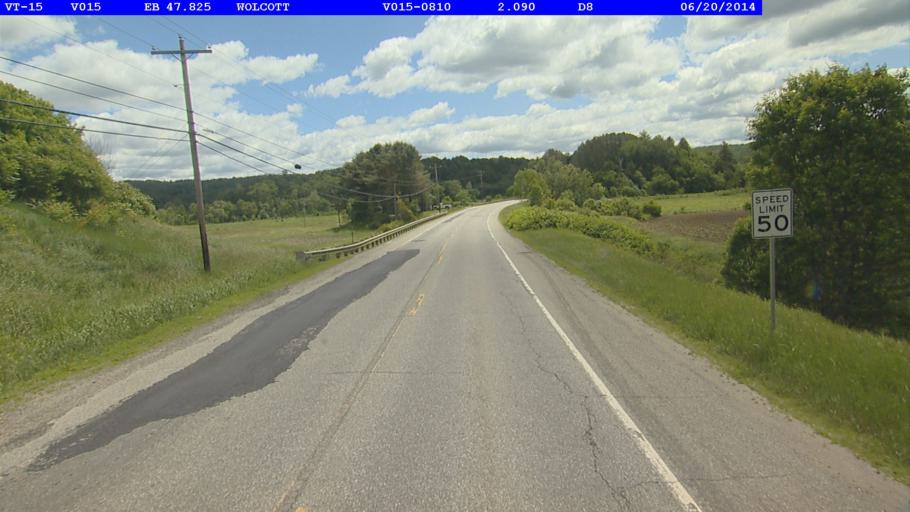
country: US
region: Vermont
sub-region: Lamoille County
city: Morrisville
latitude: 44.5632
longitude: -72.4939
